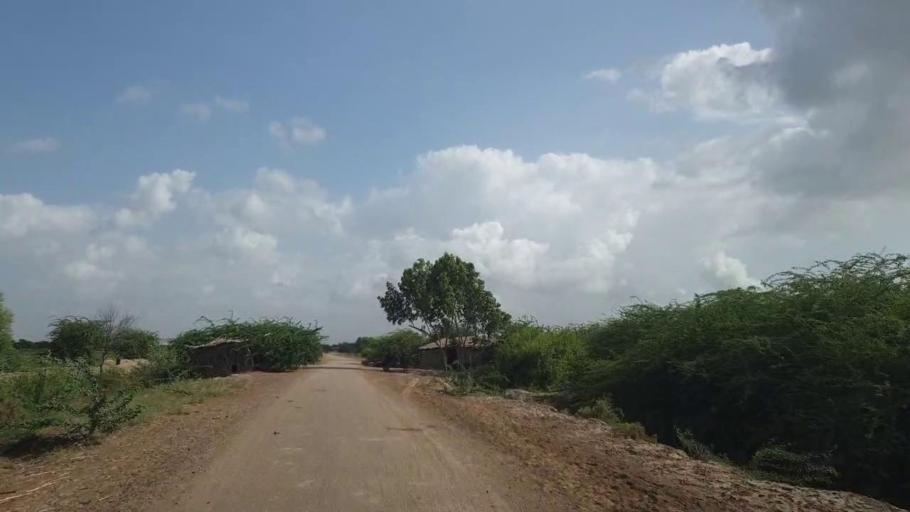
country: PK
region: Sindh
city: Kadhan
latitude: 24.5537
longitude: 69.0637
